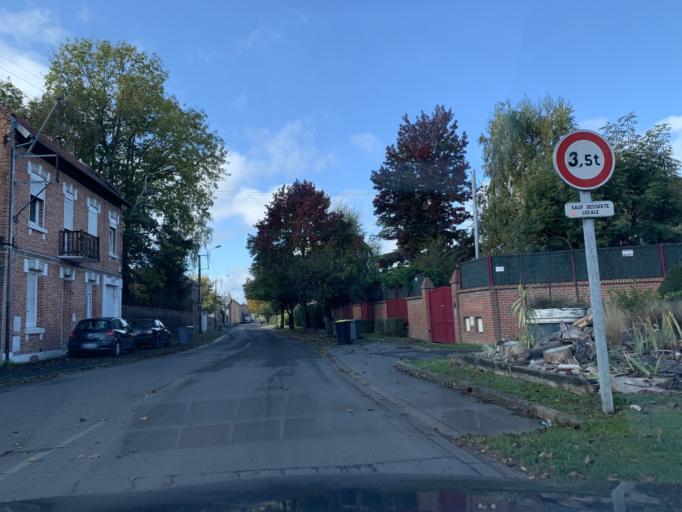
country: FR
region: Nord-Pas-de-Calais
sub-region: Departement du Nord
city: Escaudoeuvres
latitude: 50.1857
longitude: 3.2481
